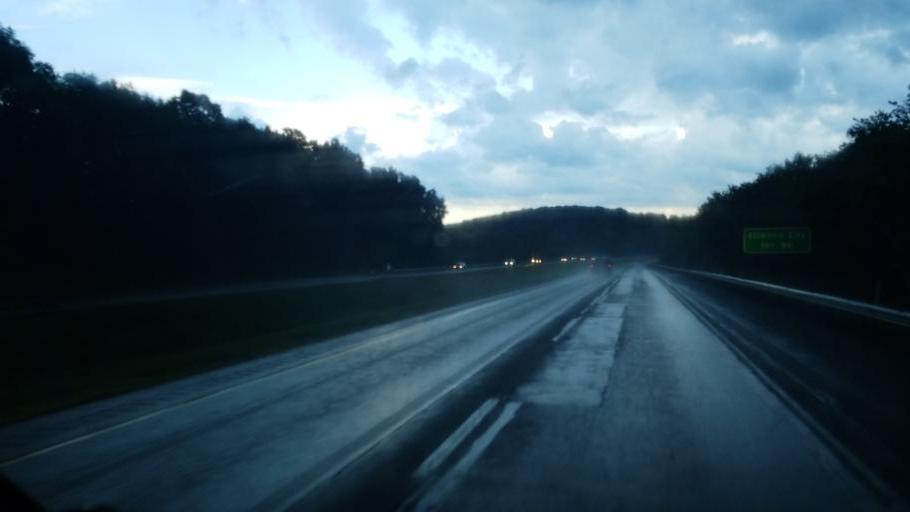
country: US
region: Pennsylvania
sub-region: Butler County
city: Prospect
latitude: 40.9436
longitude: -80.1406
